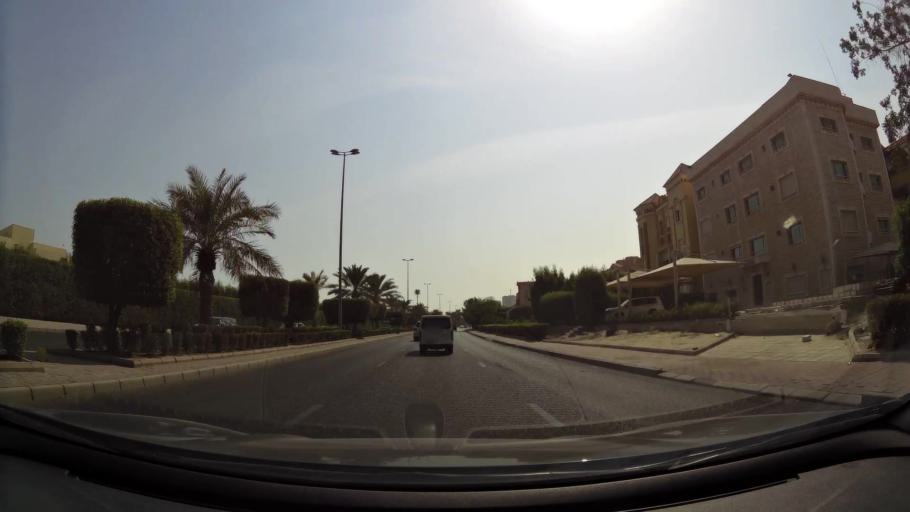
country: KW
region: Al Ahmadi
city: Al Manqaf
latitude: 29.1113
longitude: 48.1363
